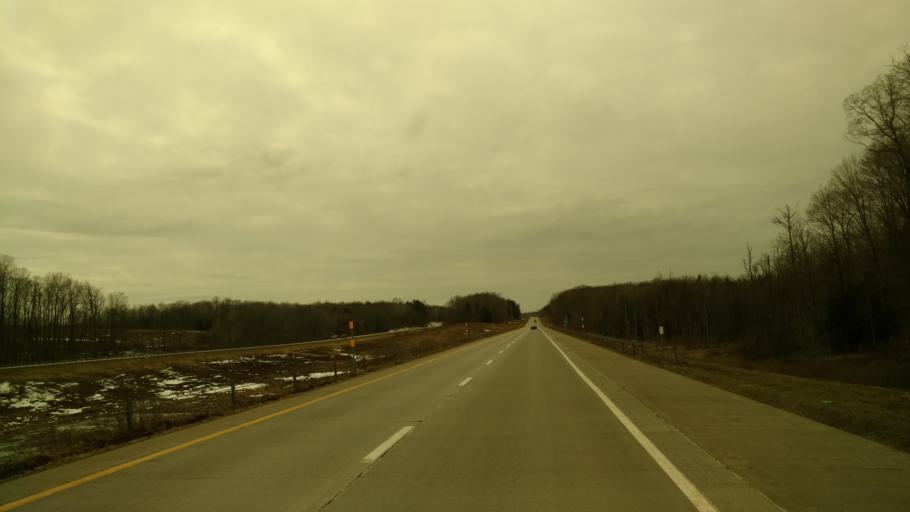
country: US
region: New York
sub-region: Chautauqua County
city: Mayville
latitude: 42.1545
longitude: -79.4489
